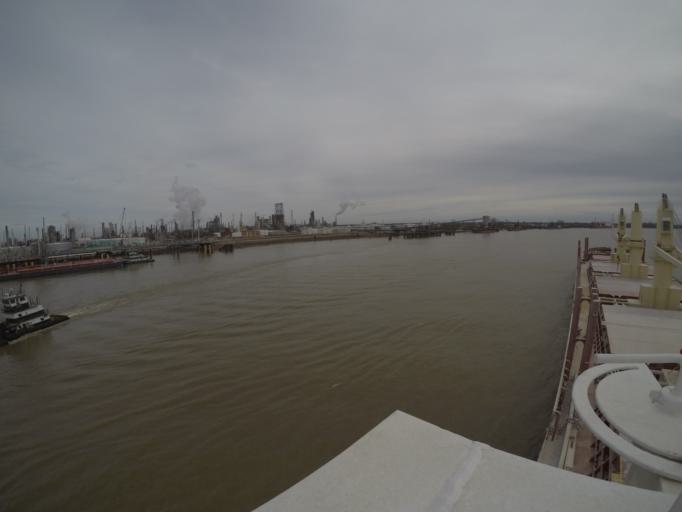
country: US
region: Louisiana
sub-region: Saint Charles Parish
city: Norco
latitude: 29.9914
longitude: -90.4094
